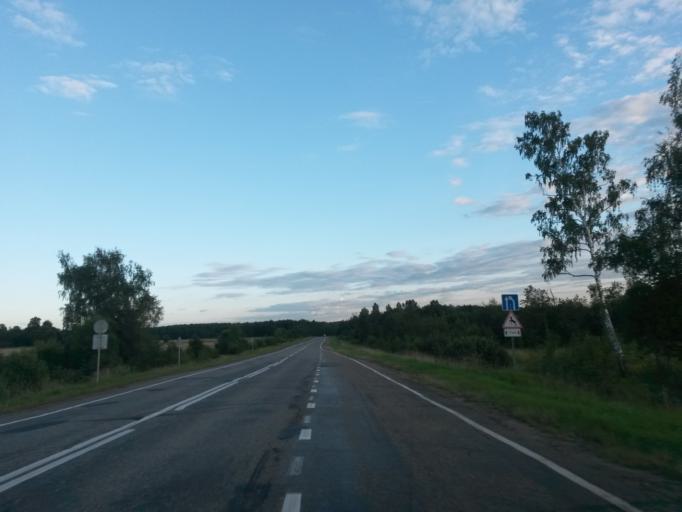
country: RU
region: Jaroslavl
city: Gavrilov-Yam
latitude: 57.4450
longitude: 39.9154
